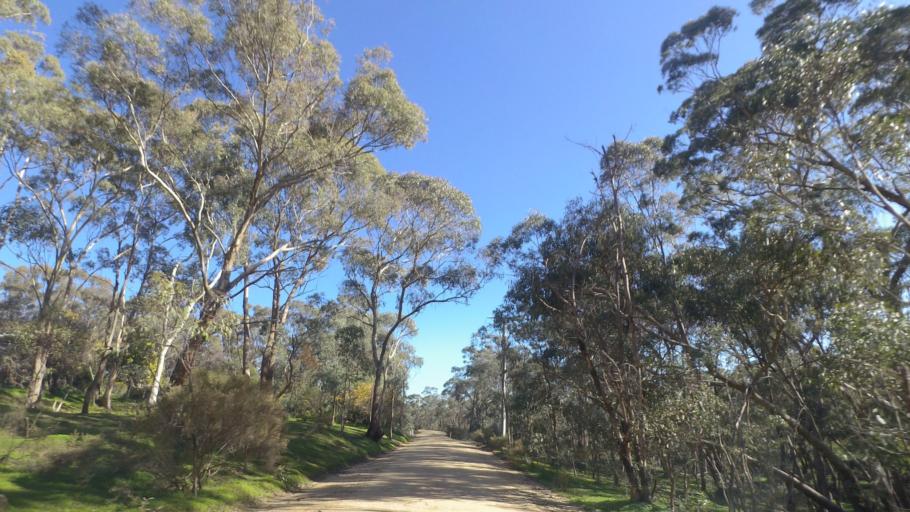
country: AU
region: Victoria
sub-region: Mount Alexander
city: Castlemaine
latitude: -37.0314
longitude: 144.2552
